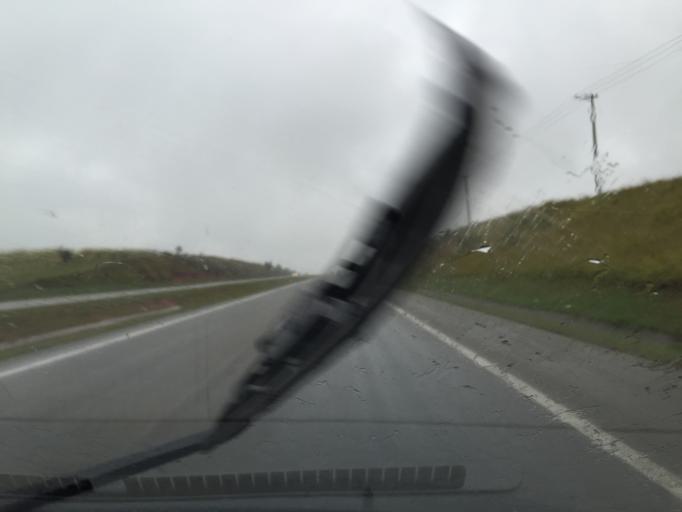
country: BR
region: Sao Paulo
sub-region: Itu
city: Itu
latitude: -23.3449
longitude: -47.3250
